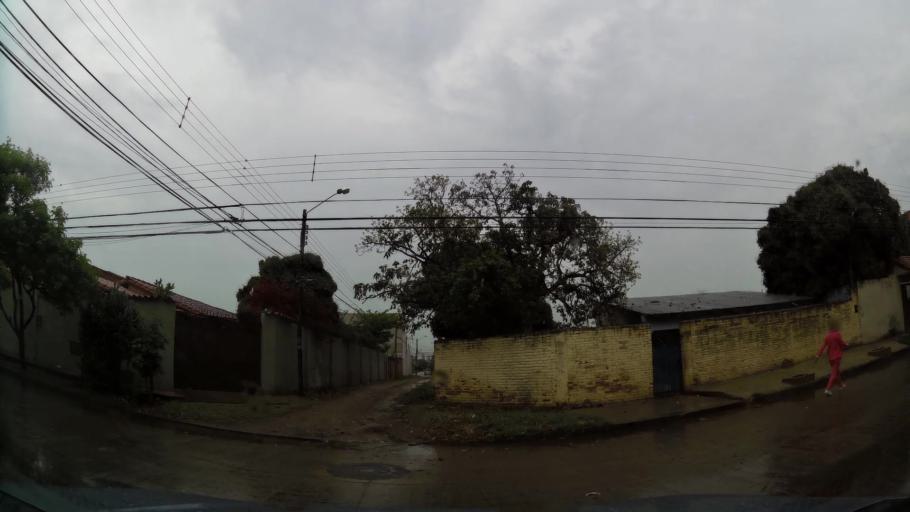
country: BO
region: Santa Cruz
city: Santa Cruz de la Sierra
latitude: -17.7930
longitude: -63.2098
